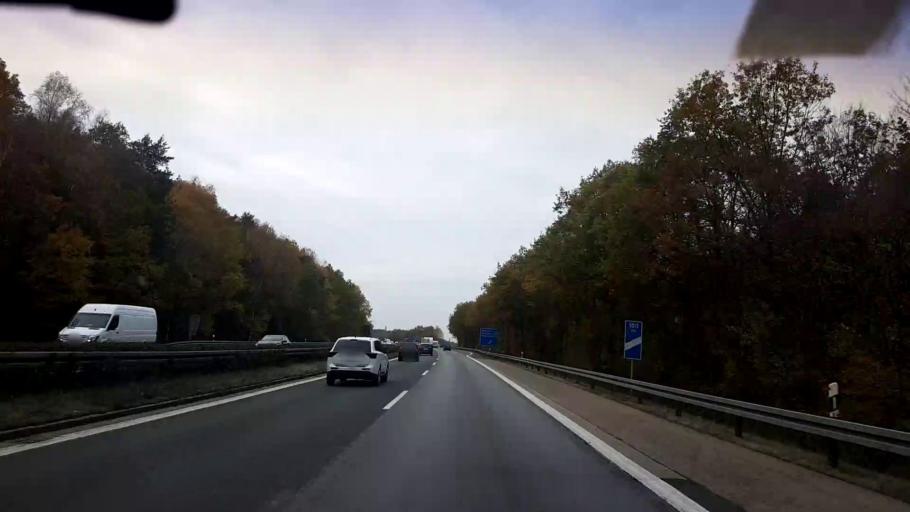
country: DE
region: Bavaria
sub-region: Regierungsbezirk Mittelfranken
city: Muhlhausen
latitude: 49.7376
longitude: 10.7983
